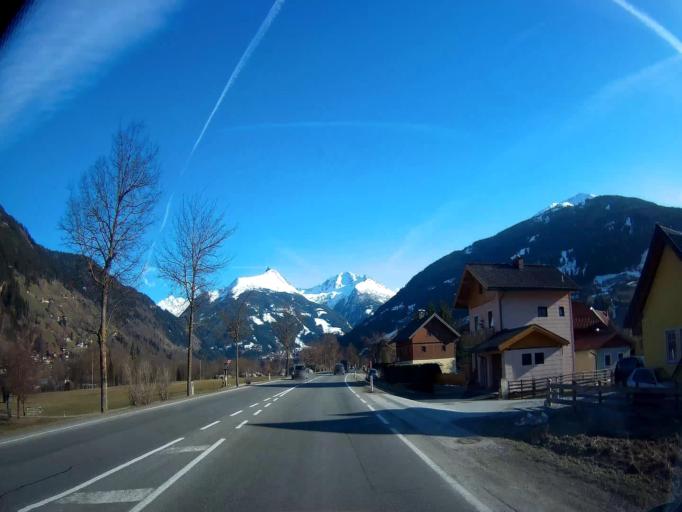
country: AT
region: Salzburg
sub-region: Politischer Bezirk Sankt Johann im Pongau
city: Bad Hofgastein
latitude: 47.1538
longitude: 13.1116
